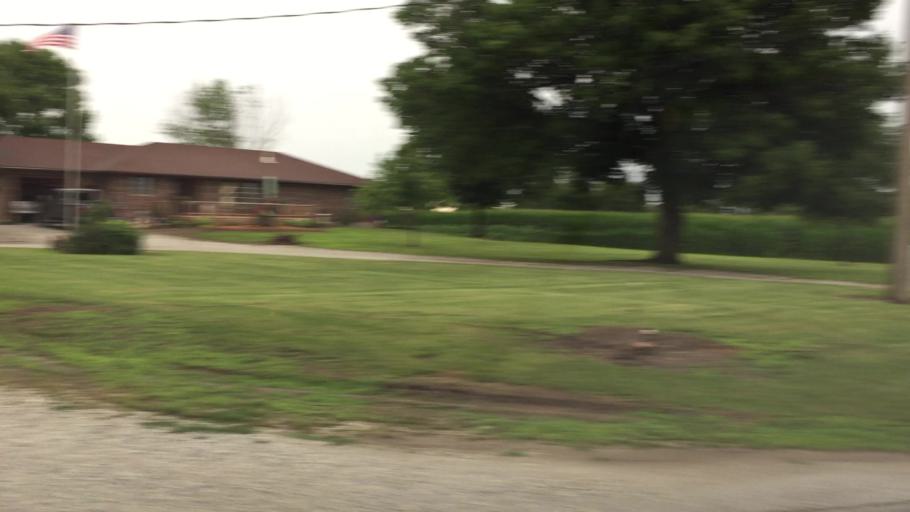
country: US
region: Illinois
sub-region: Hancock County
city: Hamilton
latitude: 40.4260
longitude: -91.3365
